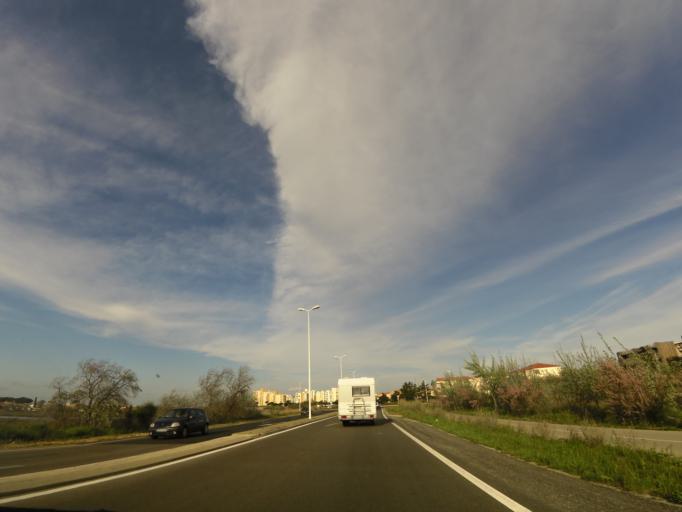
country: FR
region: Languedoc-Roussillon
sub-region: Departement de l'Herault
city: Perols
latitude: 43.5438
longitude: 3.9669
